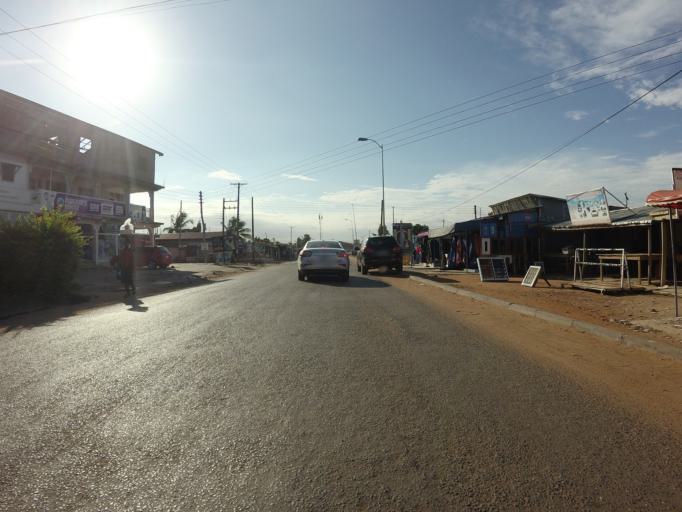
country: GH
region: Greater Accra
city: Nungua
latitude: 5.6473
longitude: -0.0609
